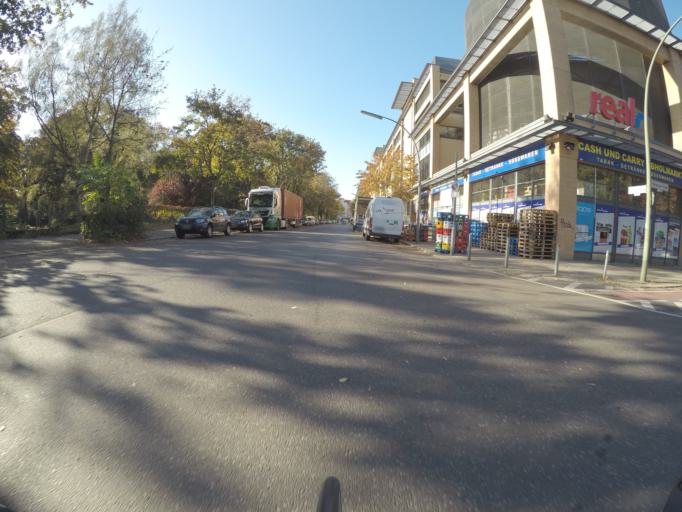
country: DE
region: Berlin
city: Wedding Bezirk
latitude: 52.5534
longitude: 13.3530
